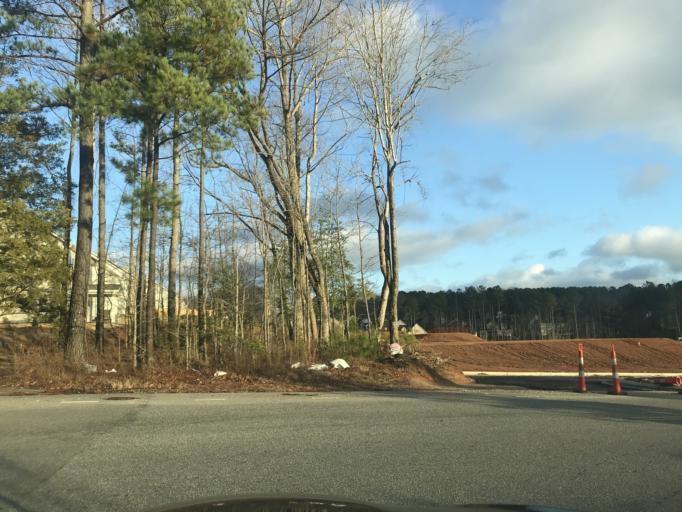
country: US
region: North Carolina
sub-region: Wake County
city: Wake Forest
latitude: 35.9594
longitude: -78.5340
